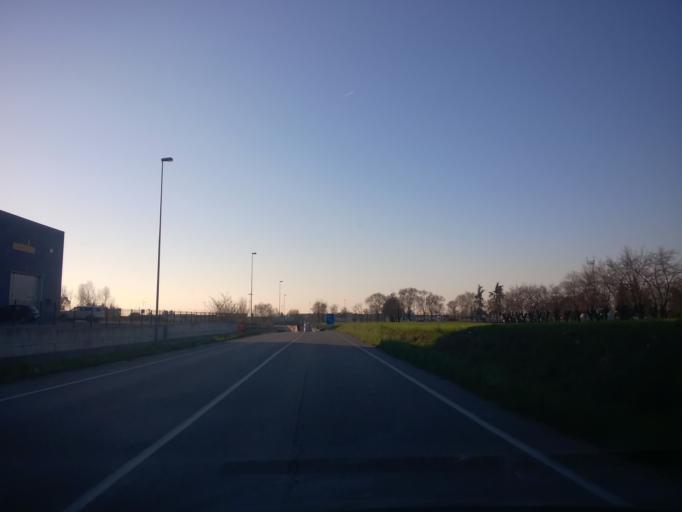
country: IT
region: Veneto
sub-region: Provincia di Vicenza
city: Thiene
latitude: 45.6862
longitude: 11.4634
